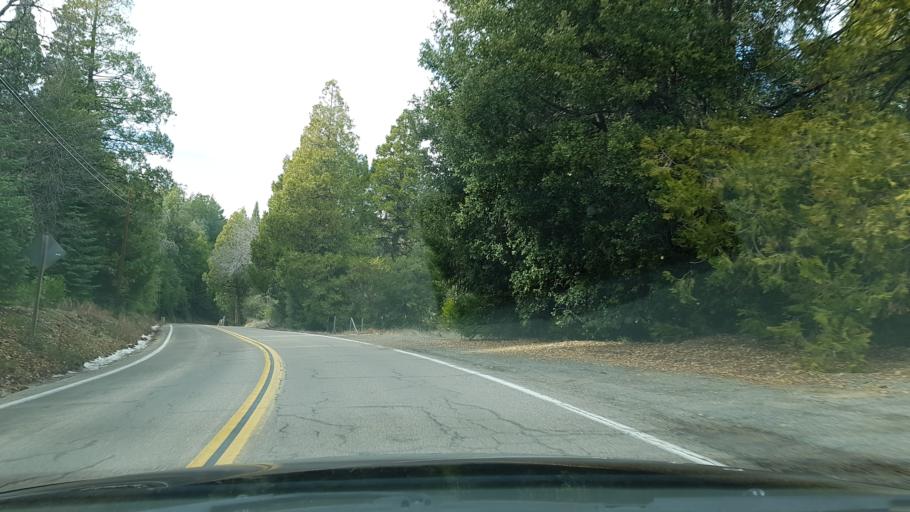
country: US
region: California
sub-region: Riverside County
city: Aguanga
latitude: 33.3313
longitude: -116.8697
